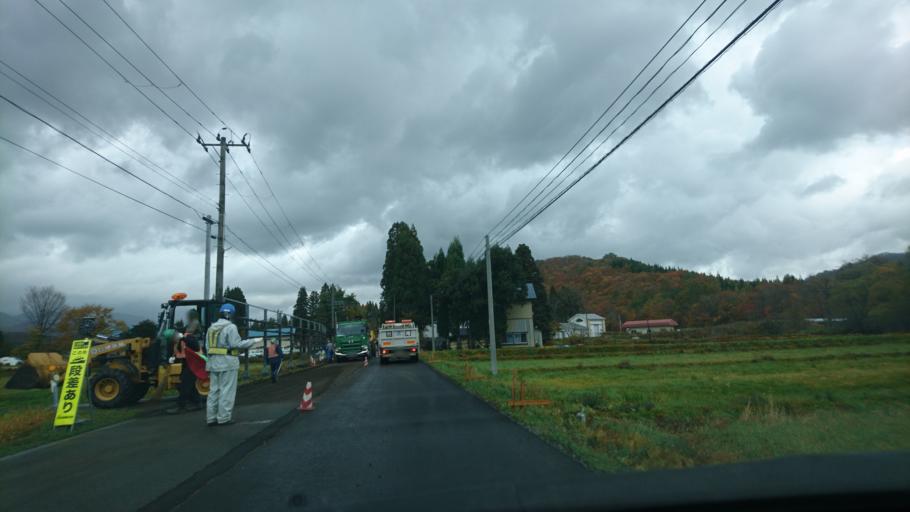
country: JP
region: Iwate
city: Shizukuishi
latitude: 39.5152
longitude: 140.8295
